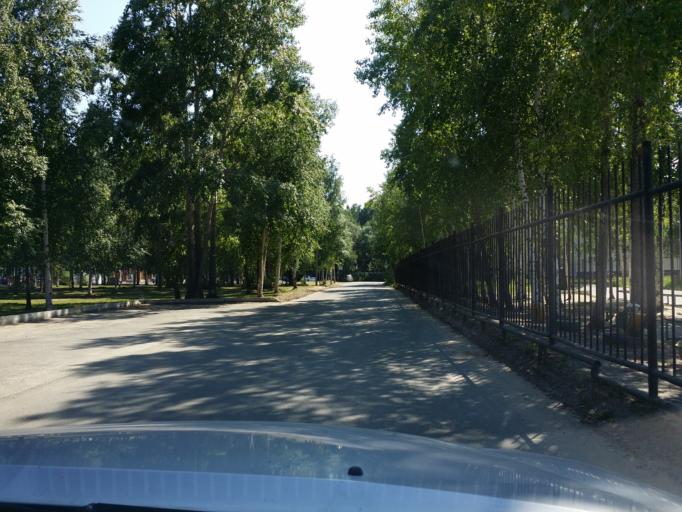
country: RU
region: Tomsk
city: Strezhevoy
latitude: 60.7263
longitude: 77.6024
